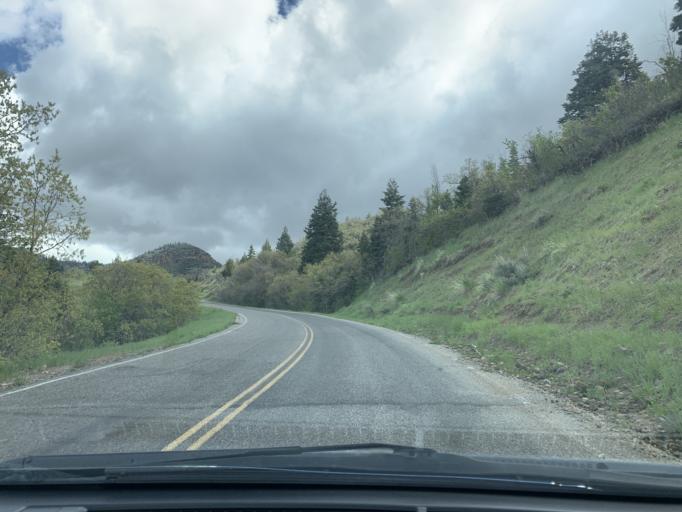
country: US
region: Utah
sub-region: Sanpete County
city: Fountain Green
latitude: 39.7818
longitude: -111.6907
